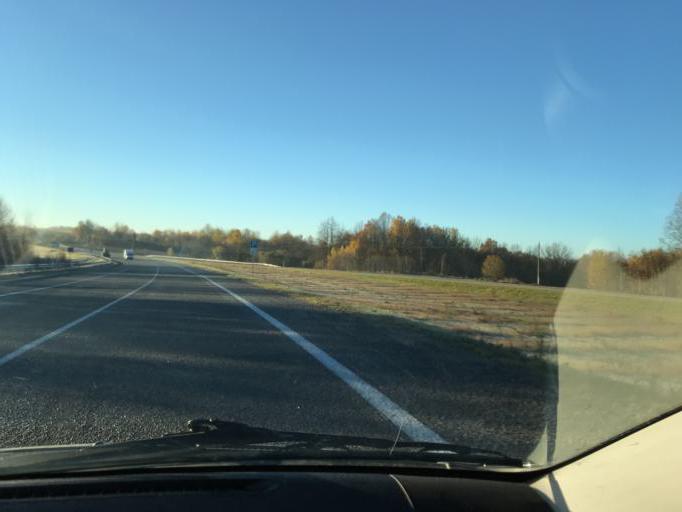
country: BY
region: Vitebsk
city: Vitebsk
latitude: 55.1001
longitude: 30.2997
